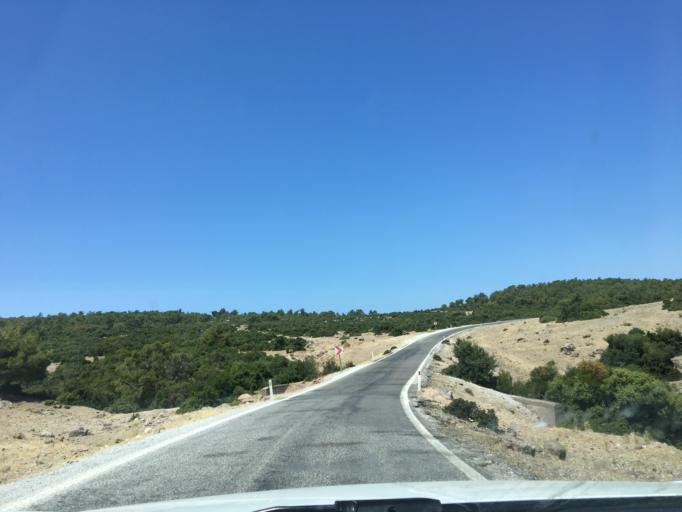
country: TR
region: Canakkale
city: Gulpinar
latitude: 39.4955
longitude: 26.1450
